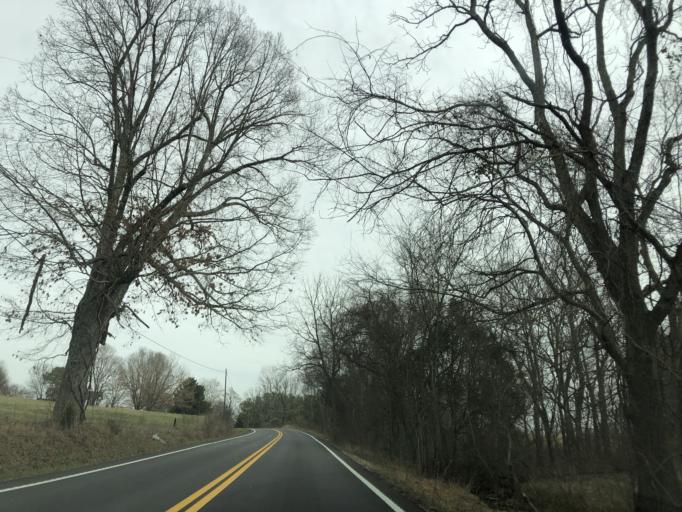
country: US
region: Tennessee
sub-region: Robertson County
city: Greenbrier
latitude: 36.4744
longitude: -86.7415
